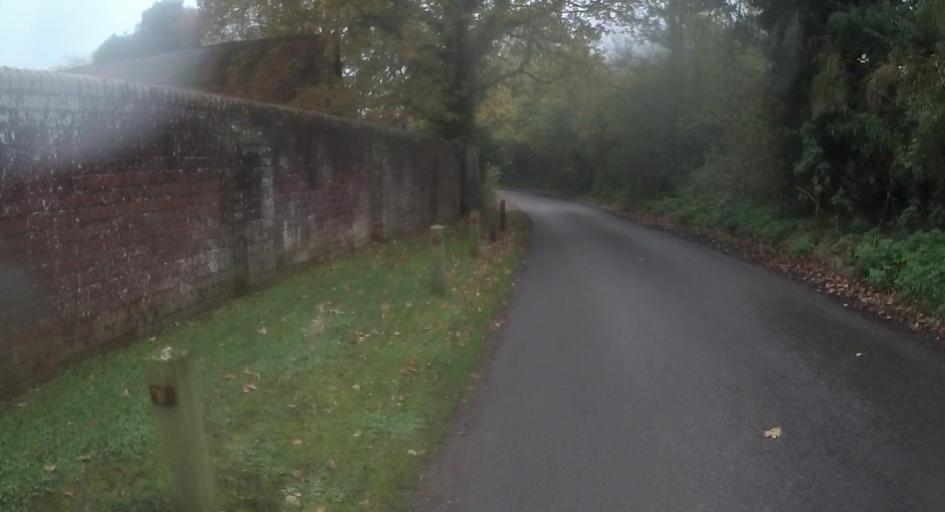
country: GB
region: England
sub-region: Wokingham
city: Finchampstead
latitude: 51.3692
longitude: -0.8626
